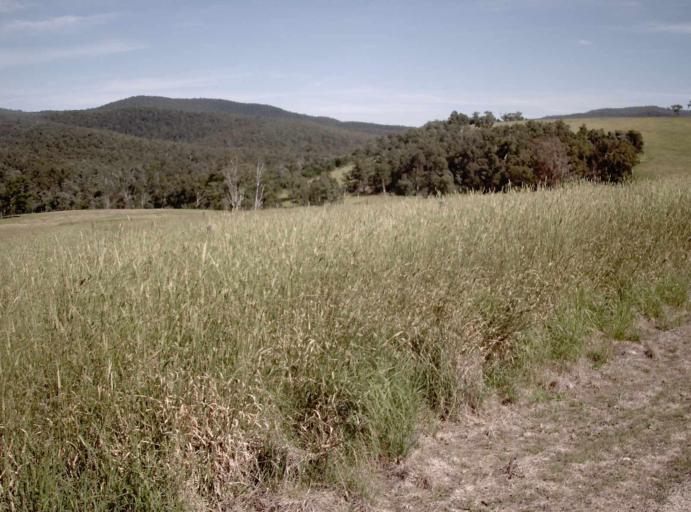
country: AU
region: Victoria
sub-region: East Gippsland
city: Lakes Entrance
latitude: -37.5008
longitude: 148.1328
